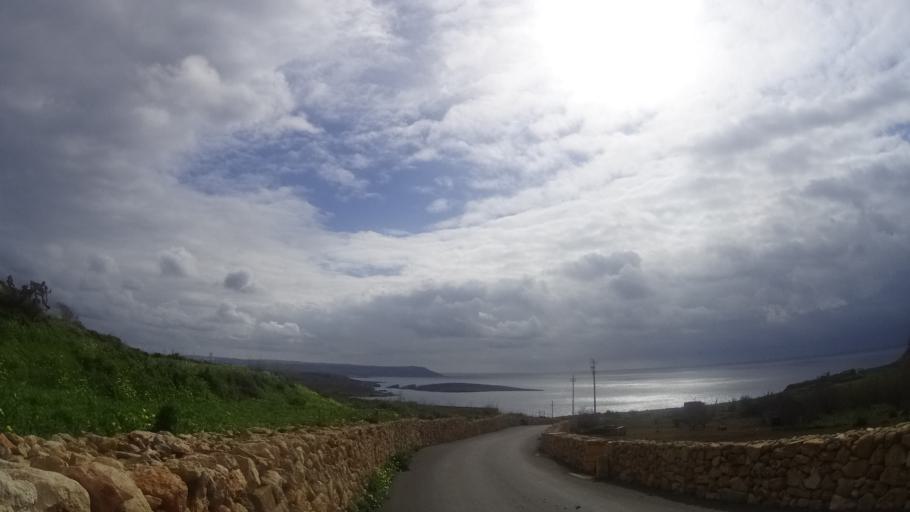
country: MT
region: Il-Qala
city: Qala
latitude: 36.0319
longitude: 14.3216
